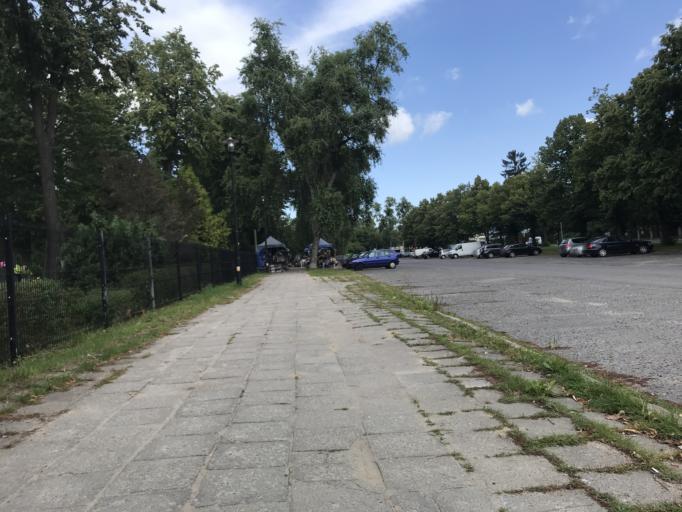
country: PL
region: Warmian-Masurian Voivodeship
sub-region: Powiat elblaski
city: Elblag
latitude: 54.1682
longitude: 19.4238
